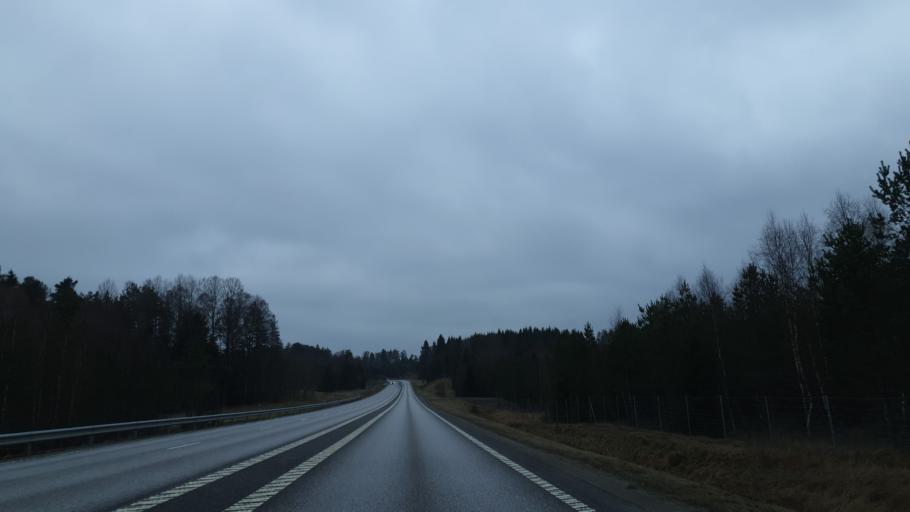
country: SE
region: Vaestra Goetaland
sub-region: Boras Kommun
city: Viskafors
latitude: 57.5995
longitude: 12.8714
